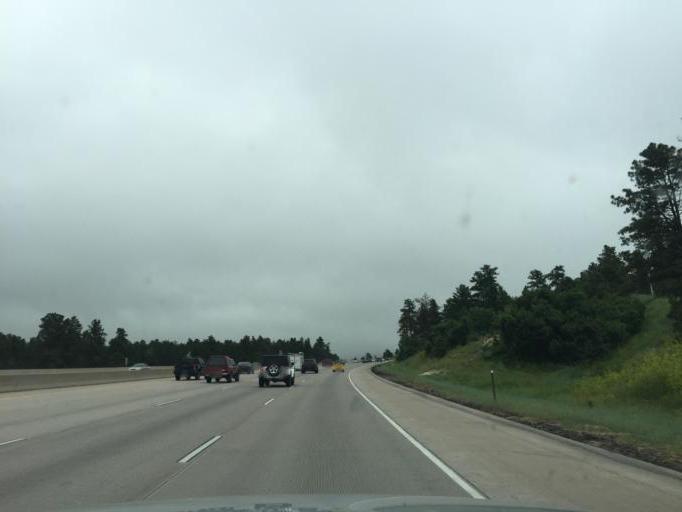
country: US
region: Colorado
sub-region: Douglas County
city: Castle Pines
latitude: 39.4361
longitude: -104.8784
